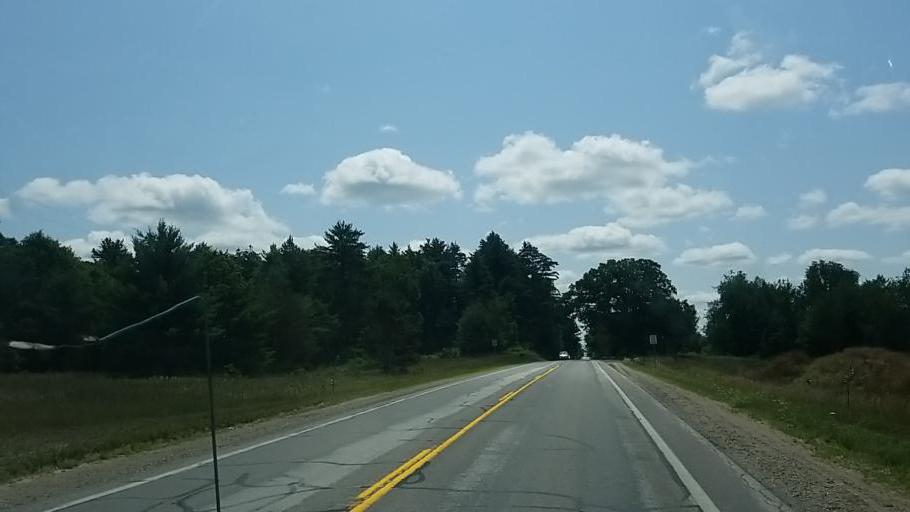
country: US
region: Michigan
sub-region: Newaygo County
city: Fremont
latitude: 43.4807
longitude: -86.0396
